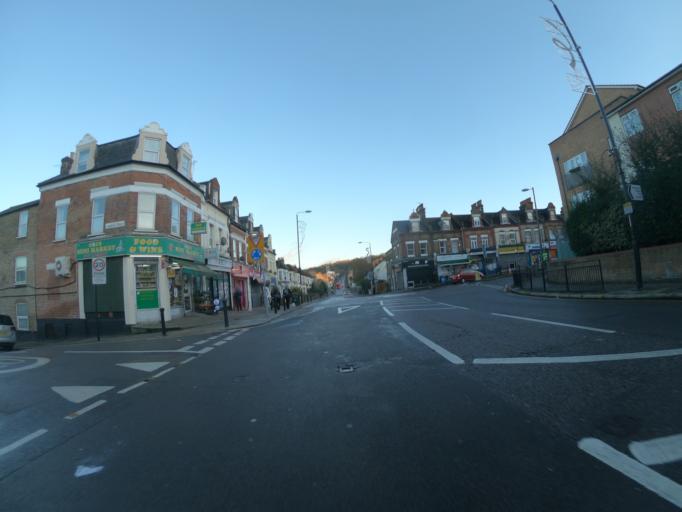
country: GB
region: England
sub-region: Greater London
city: Abbey Wood
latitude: 51.4856
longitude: 0.1023
